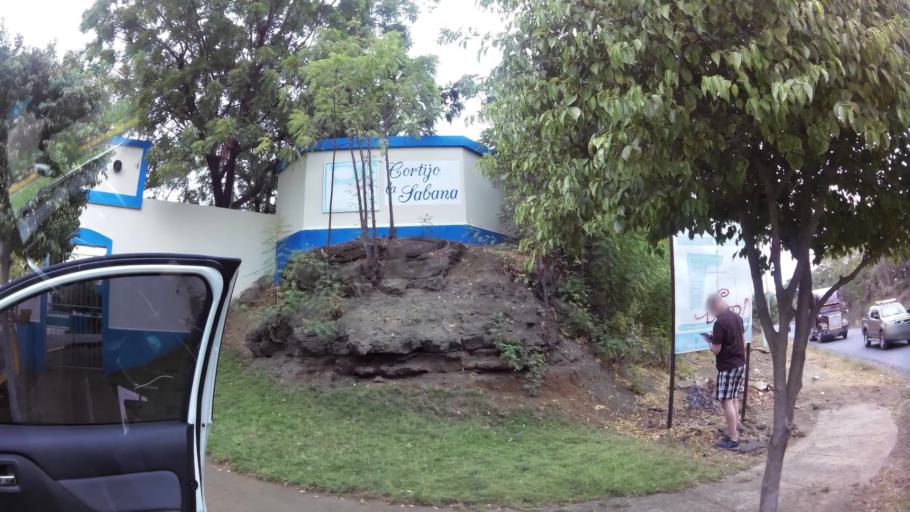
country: NI
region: Managua
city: Managua
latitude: 12.1239
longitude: -86.1837
